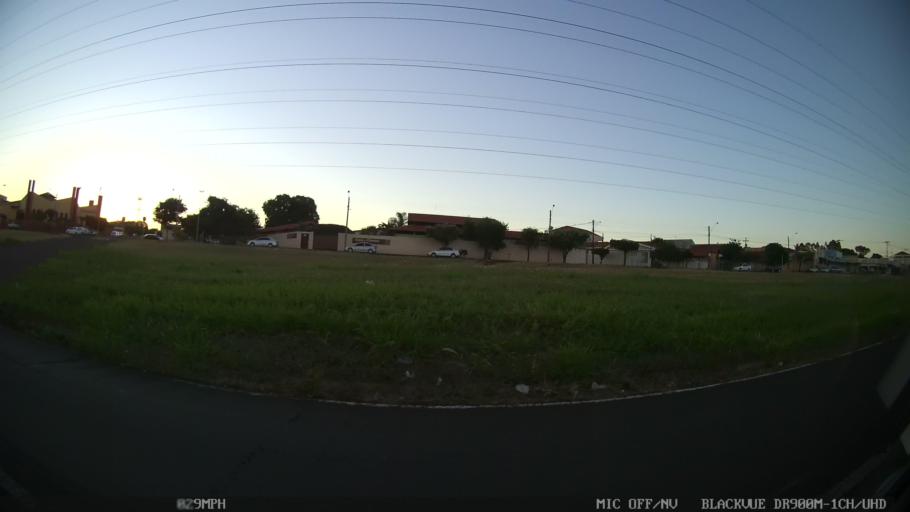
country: BR
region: Sao Paulo
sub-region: Sao Jose Do Rio Preto
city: Sao Jose do Rio Preto
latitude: -20.8437
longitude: -49.3774
